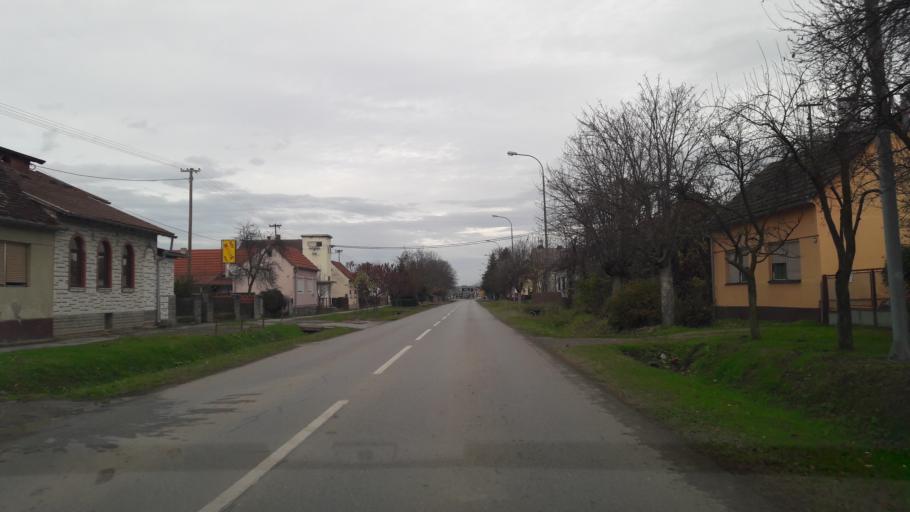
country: HR
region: Virovitick-Podravska
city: Orahovica
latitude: 45.5453
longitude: 17.9003
